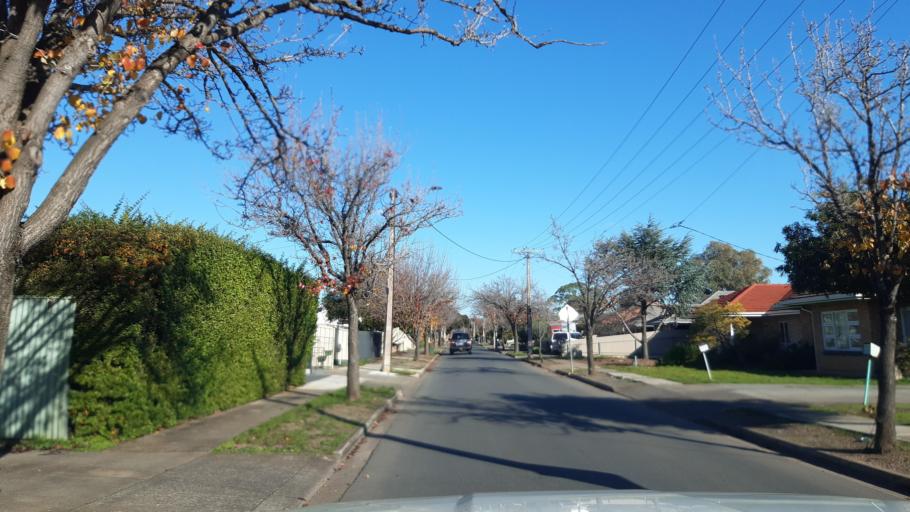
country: AU
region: South Australia
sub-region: Marion
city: Clovelly Park
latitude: -34.9893
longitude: 138.5663
